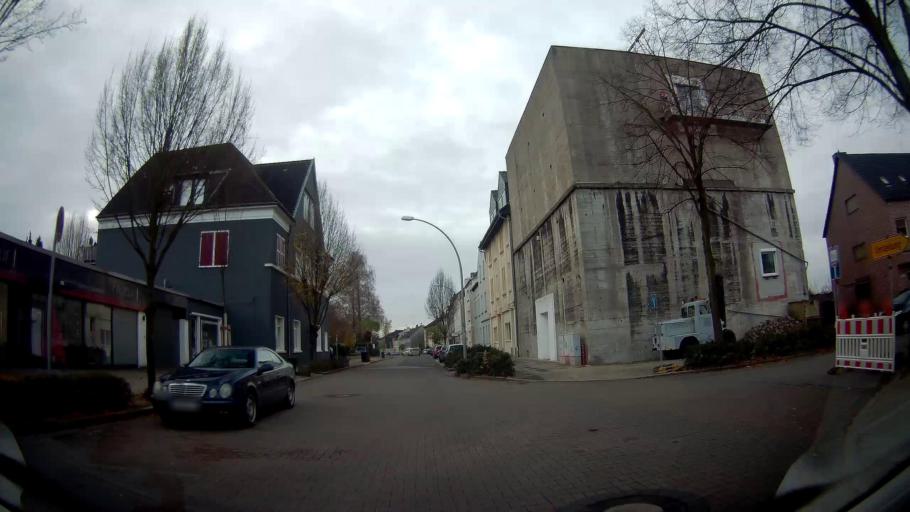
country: DE
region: North Rhine-Westphalia
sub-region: Regierungsbezirk Munster
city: Gladbeck
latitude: 51.5906
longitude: 7.0010
